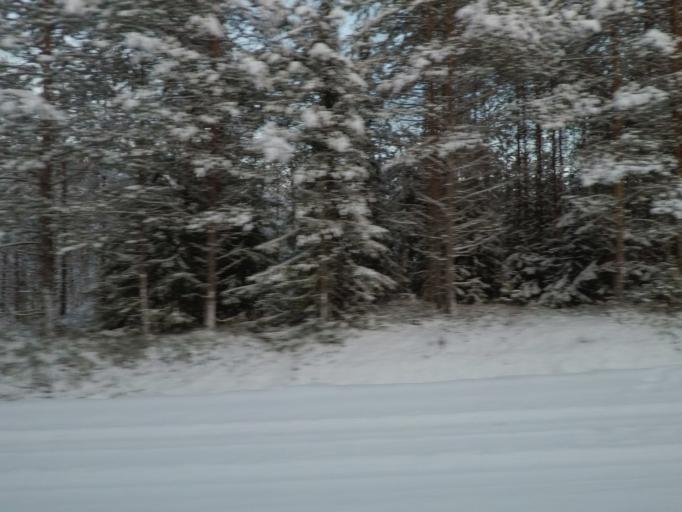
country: FI
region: Varsinais-Suomi
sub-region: Salo
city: Suomusjaervi
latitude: 60.3088
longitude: 23.6452
